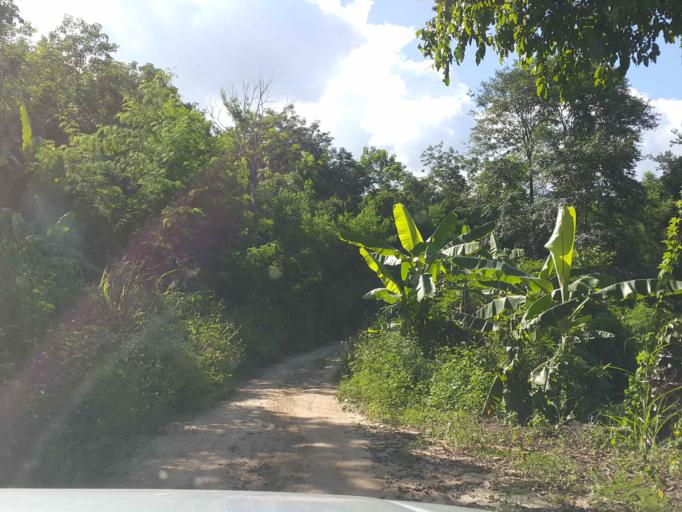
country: TH
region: Chiang Mai
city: Mae Taeng
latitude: 18.9740
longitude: 98.8856
